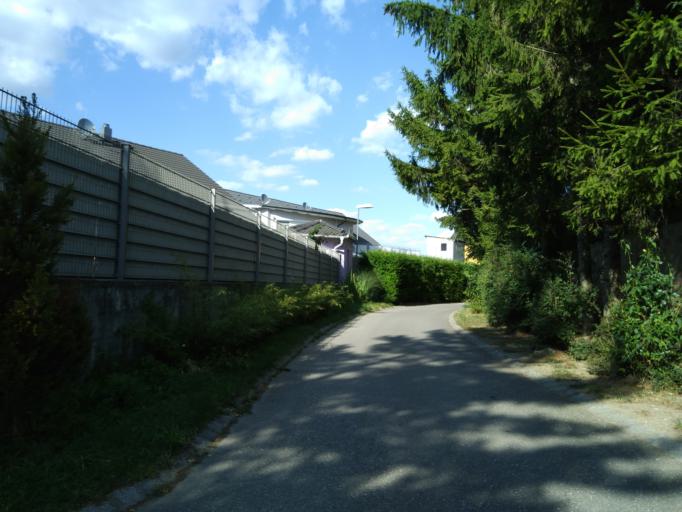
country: AT
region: Lower Austria
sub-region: Politischer Bezirk Mistelbach
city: Gross-Engersdorf
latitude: 48.3560
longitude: 16.5792
